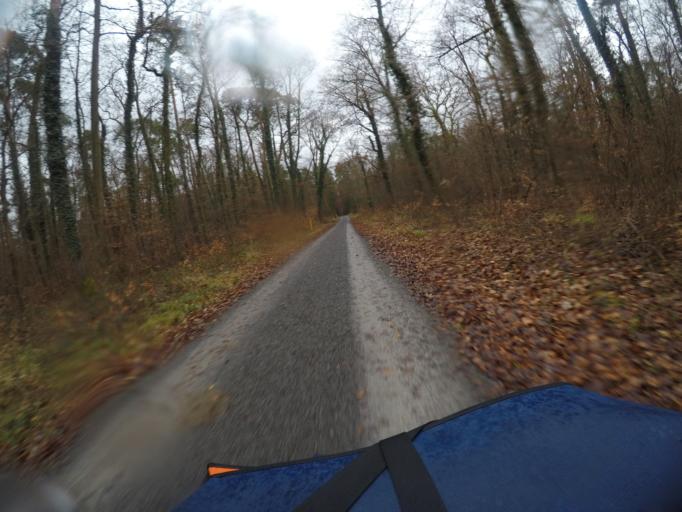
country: DE
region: Baden-Wuerttemberg
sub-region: Karlsruhe Region
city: Linkenheim-Hochstetten
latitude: 49.1376
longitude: 8.4560
